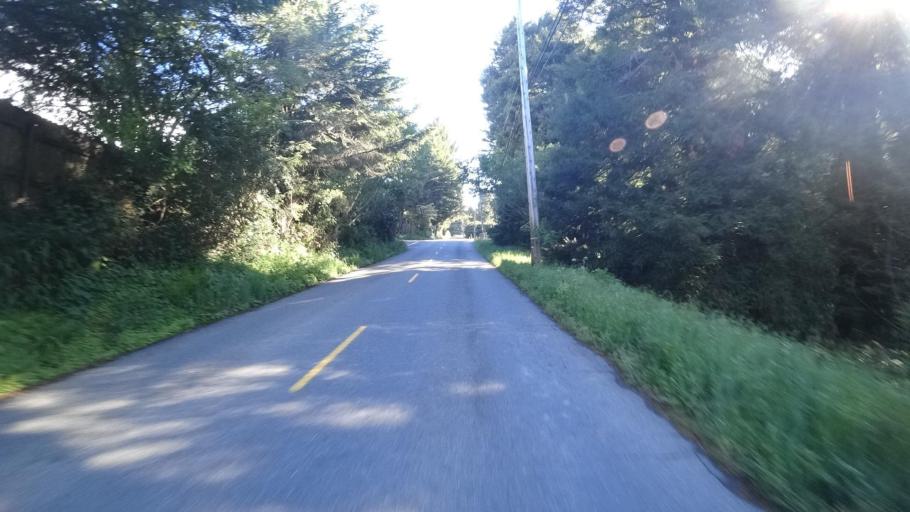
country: US
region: California
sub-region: Humboldt County
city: Westhaven-Moonstone
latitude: 41.0345
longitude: -124.1084
